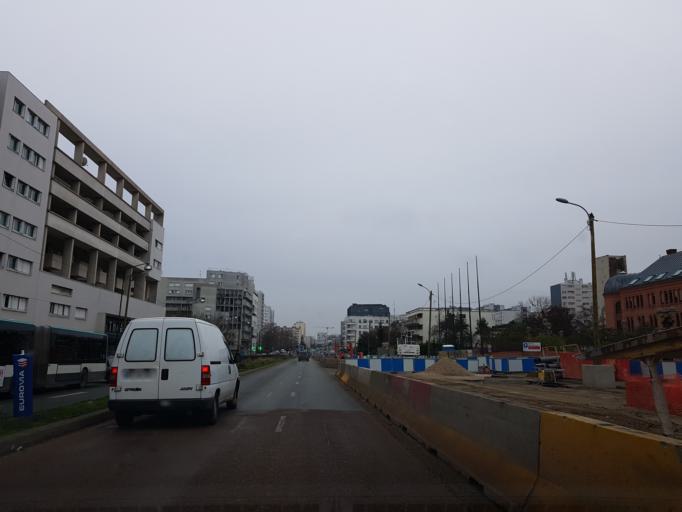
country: FR
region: Ile-de-France
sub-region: Departement du Val-de-Marne
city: Vitry-sur-Seine
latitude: 48.7893
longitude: 2.3892
